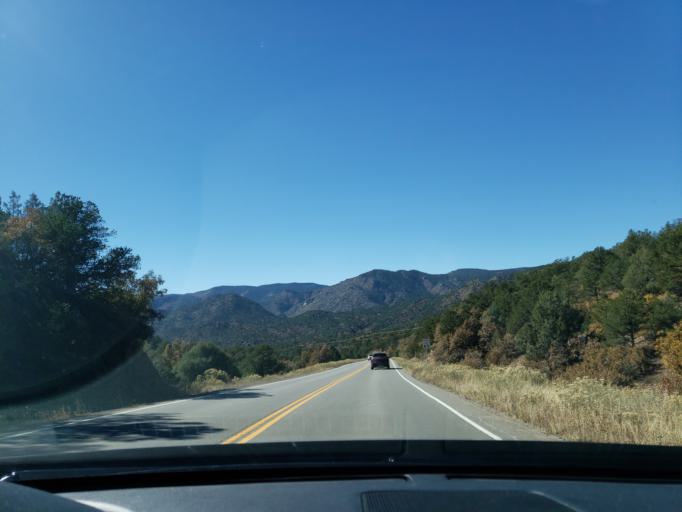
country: US
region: Colorado
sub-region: Fremont County
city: Canon City
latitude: 38.5802
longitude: -105.4174
